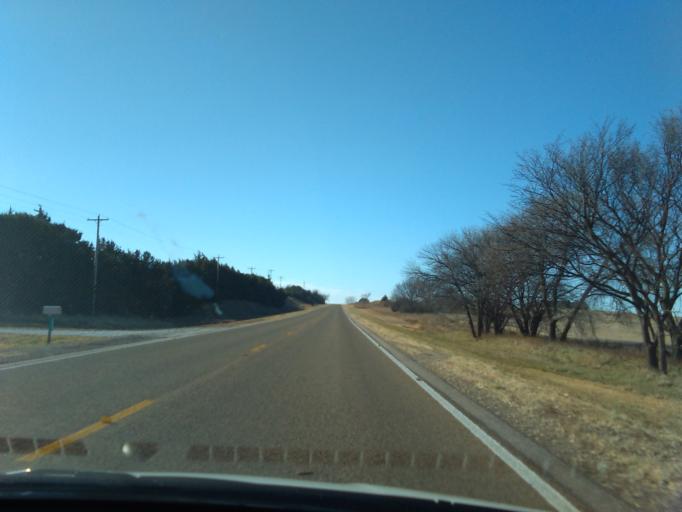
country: US
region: Nebraska
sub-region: Adams County
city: Hastings
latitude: 40.4373
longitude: -98.3650
